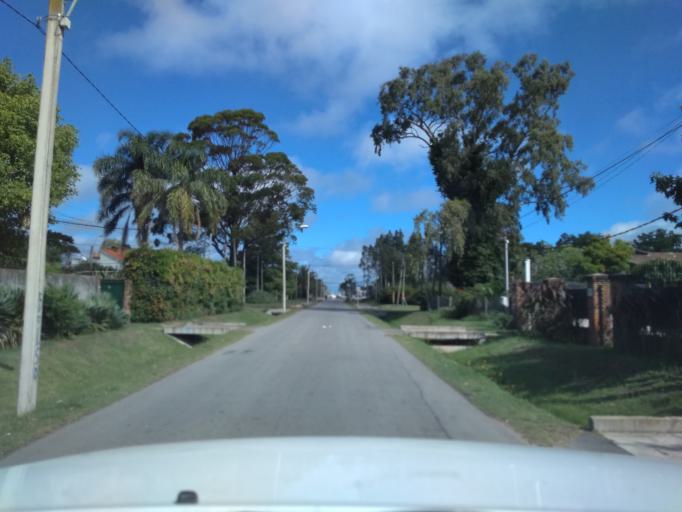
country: UY
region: Canelones
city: Barra de Carrasco
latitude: -34.8365
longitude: -55.9703
